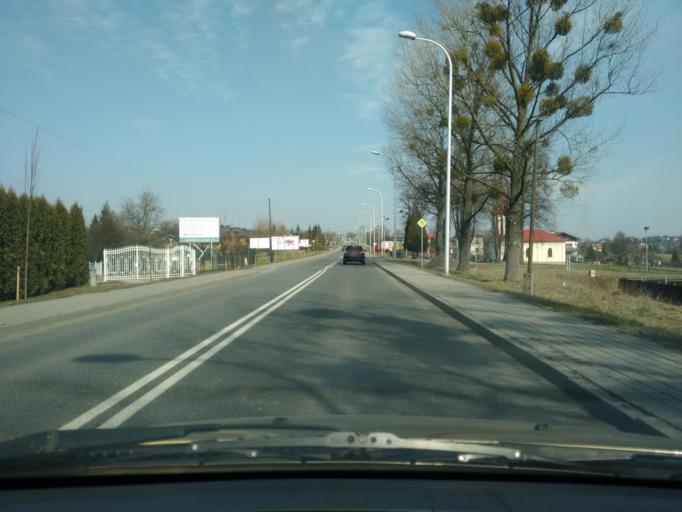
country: PL
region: Silesian Voivodeship
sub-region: Powiat cieszynski
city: Zamarski
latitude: 49.7583
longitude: 18.6800
